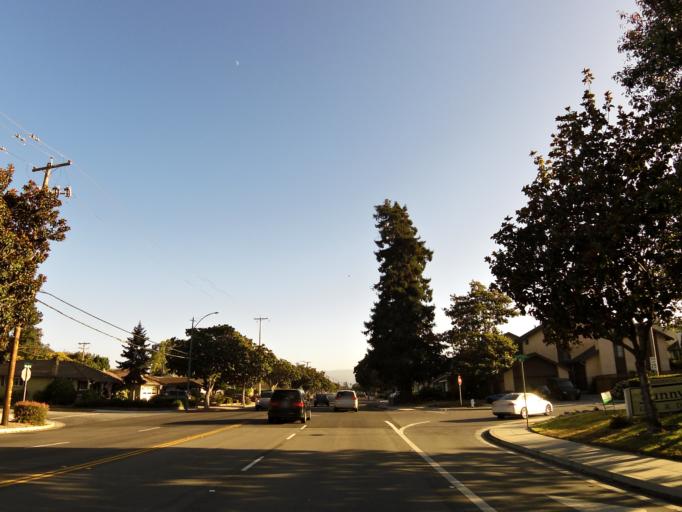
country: US
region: California
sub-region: Santa Clara County
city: Sunnyvale
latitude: 37.3814
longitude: -122.0453
